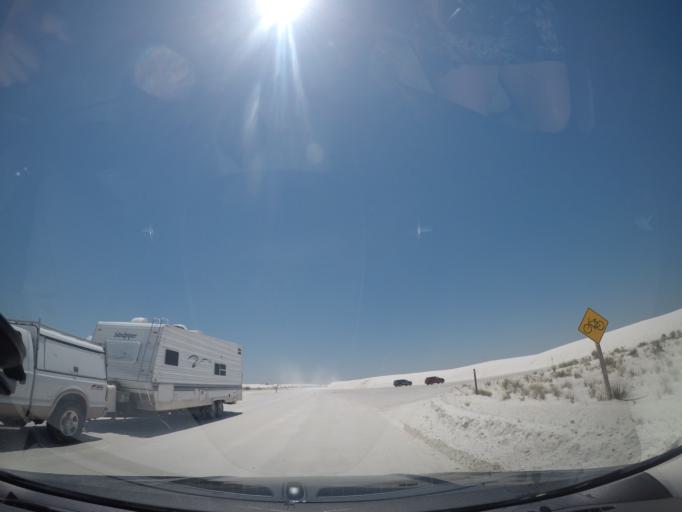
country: US
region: New Mexico
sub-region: Otero County
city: Holloman Air Force Base
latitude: 32.8069
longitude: -106.2615
